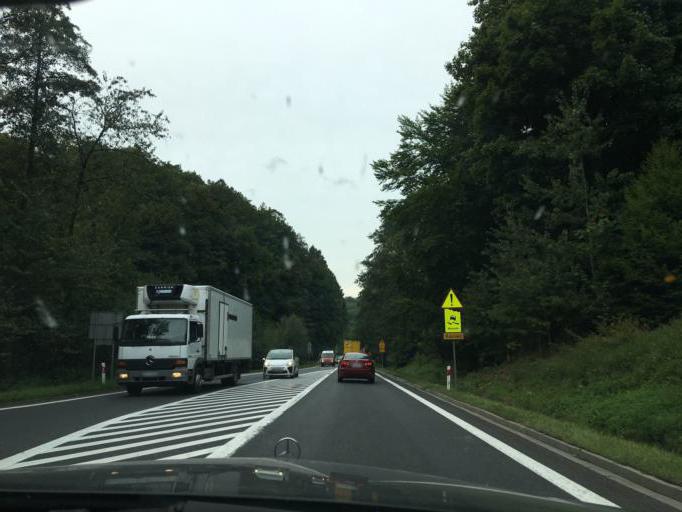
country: PL
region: Lower Silesian Voivodeship
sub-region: Powiat klodzki
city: Lewin Klodzki
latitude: 50.4074
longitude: 16.3021
